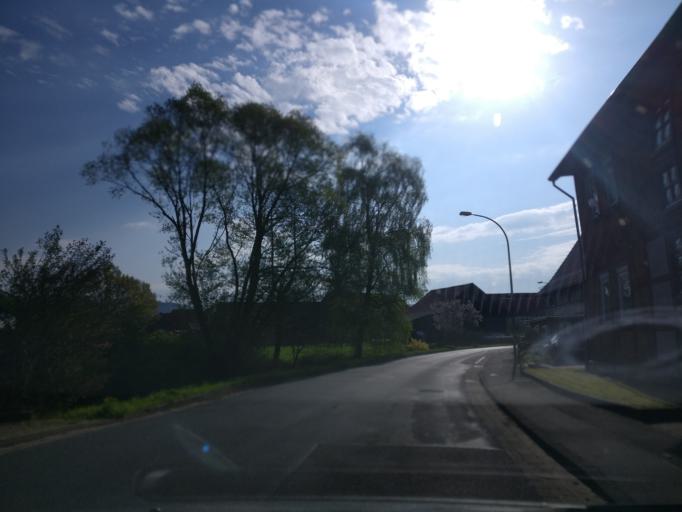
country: DE
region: Lower Saxony
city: Scheden
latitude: 51.4588
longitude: 9.7164
